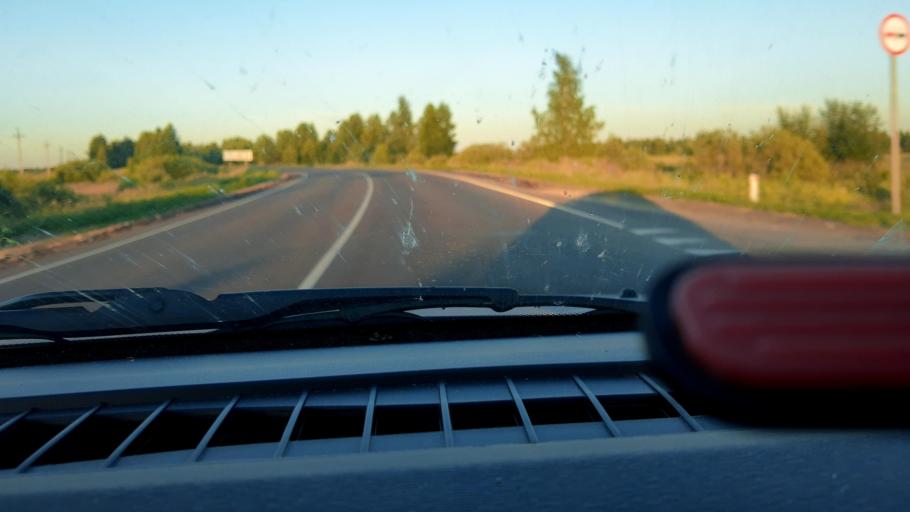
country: RU
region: Nizjnij Novgorod
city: Tonkino
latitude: 57.3448
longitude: 46.2486
